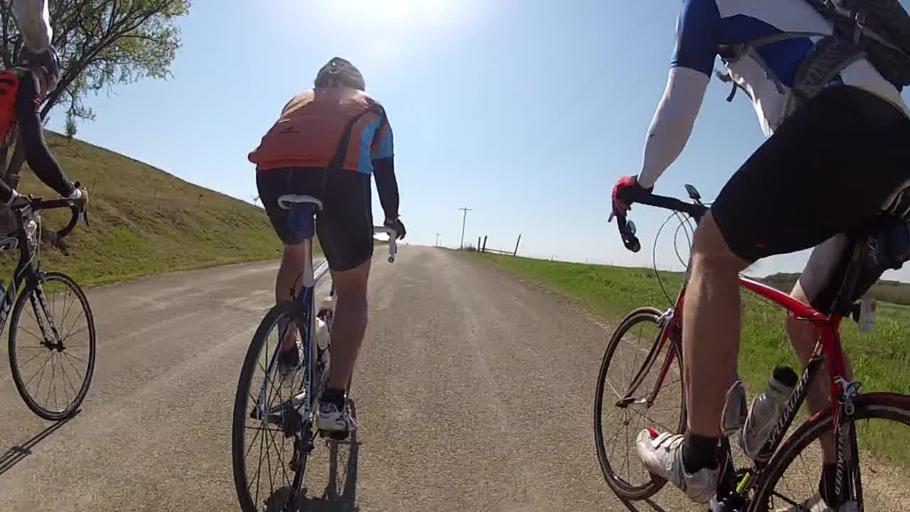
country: US
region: Kansas
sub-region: Riley County
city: Ogden
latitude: 38.9821
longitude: -96.6561
